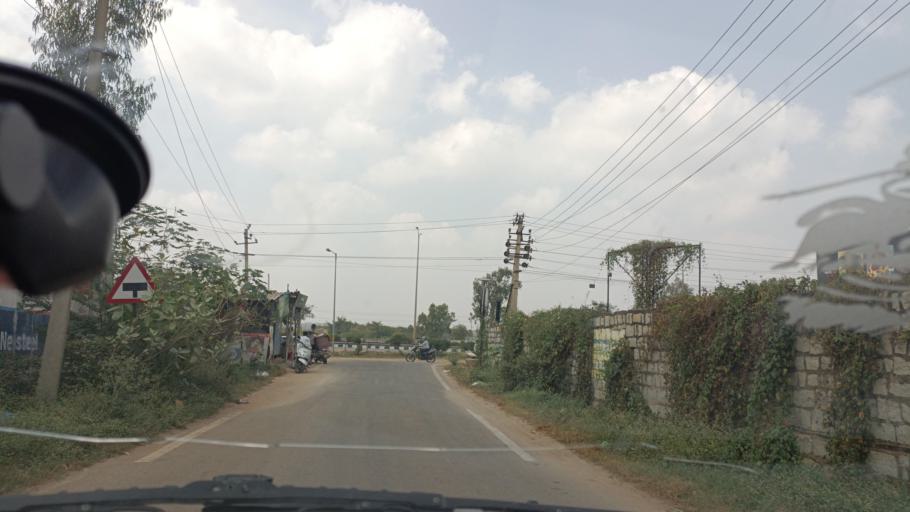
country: IN
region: Karnataka
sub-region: Bangalore Urban
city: Yelahanka
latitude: 13.1644
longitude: 77.6302
